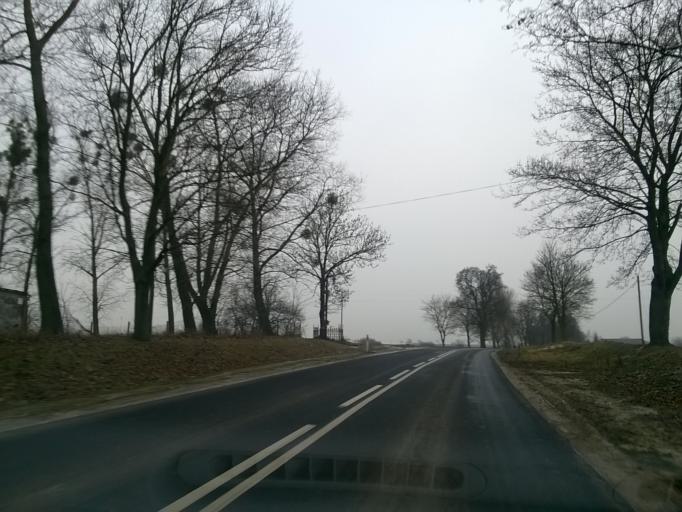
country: PL
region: Kujawsko-Pomorskie
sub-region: Powiat nakielski
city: Kcynia
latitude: 53.0233
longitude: 17.5339
